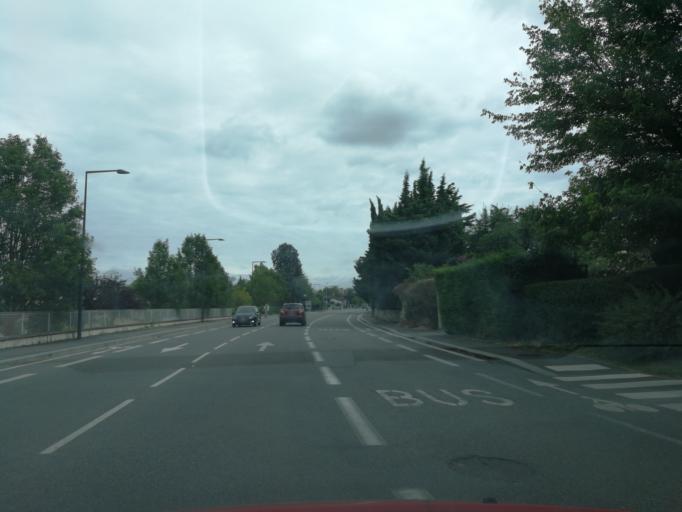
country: FR
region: Midi-Pyrenees
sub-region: Departement de la Haute-Garonne
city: Ramonville-Saint-Agne
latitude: 43.5445
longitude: 1.4764
